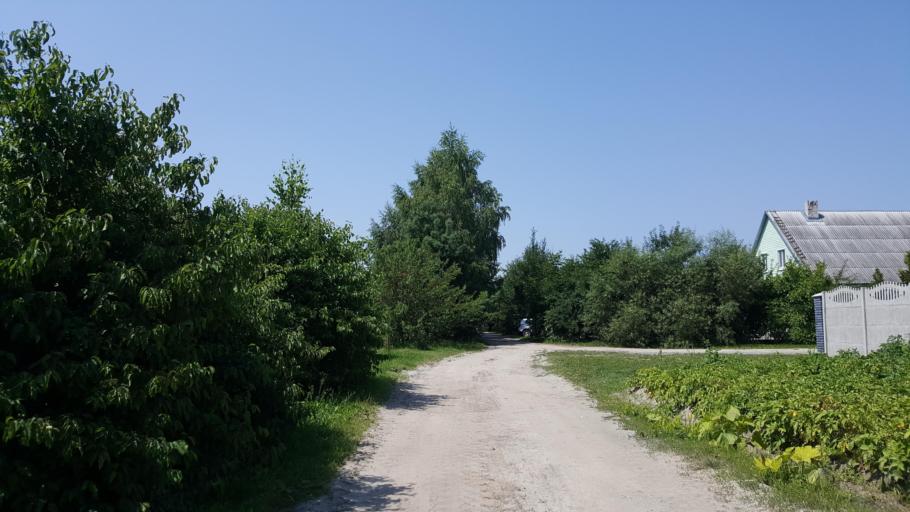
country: BY
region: Brest
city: Zhabinka
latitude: 52.1854
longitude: 23.9969
